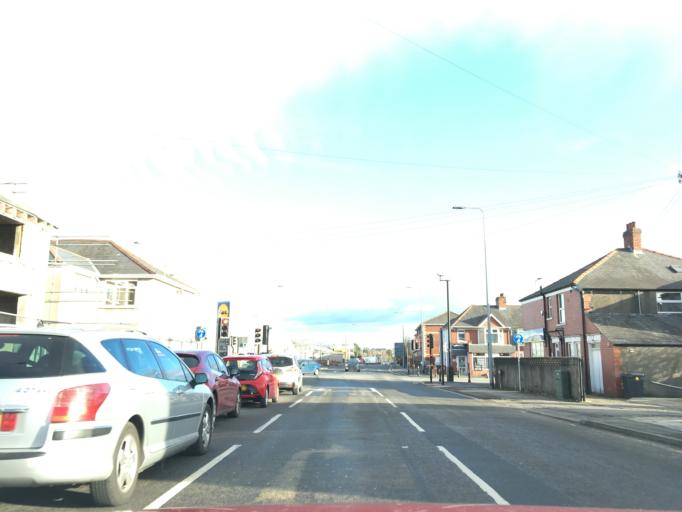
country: GB
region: Wales
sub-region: Cardiff
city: Cardiff
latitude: 51.5193
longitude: -3.2021
